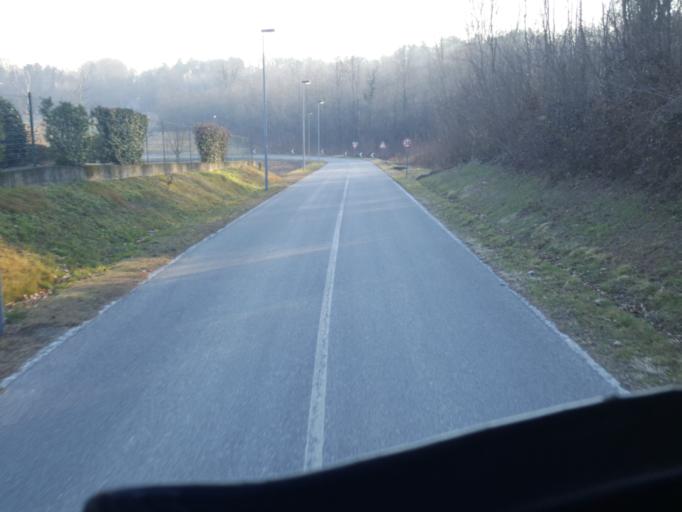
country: IT
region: Piedmont
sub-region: Provincia di Novara
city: Varallo Pombia
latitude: 45.6833
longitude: 8.6301
